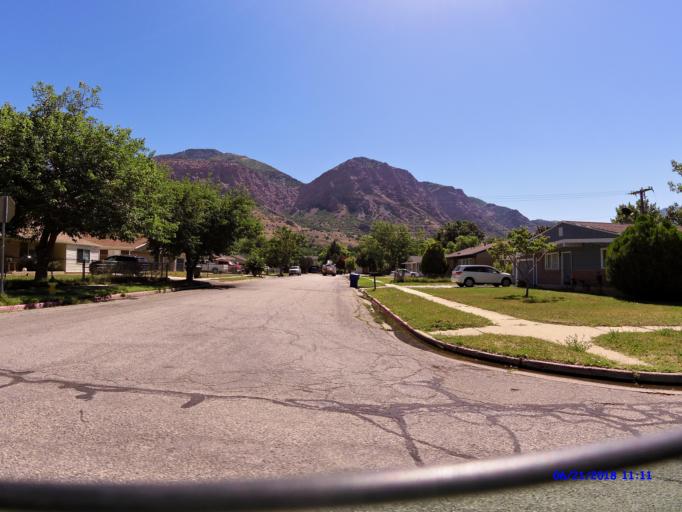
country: US
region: Utah
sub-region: Weber County
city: Harrisville
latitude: 41.2688
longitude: -111.9591
